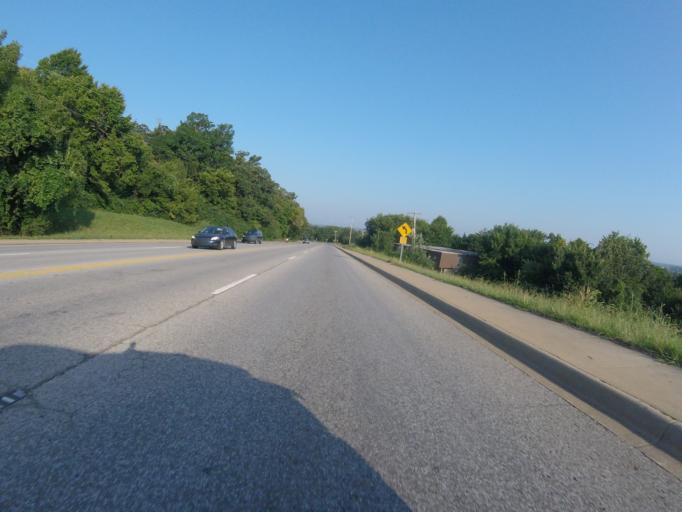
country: US
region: Arkansas
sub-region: Washington County
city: Fayetteville
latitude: 36.0785
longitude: -94.1791
